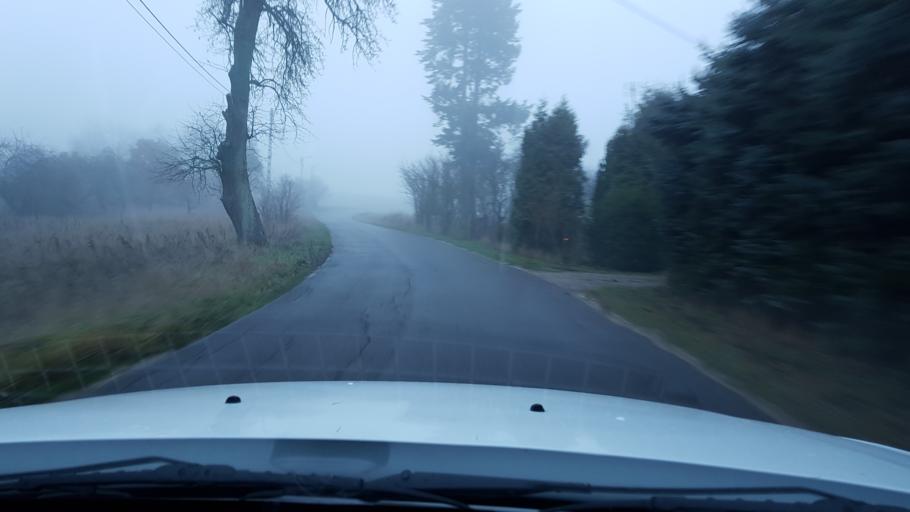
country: PL
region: West Pomeranian Voivodeship
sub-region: Powiat mysliborski
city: Mysliborz
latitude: 52.9046
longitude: 14.8219
